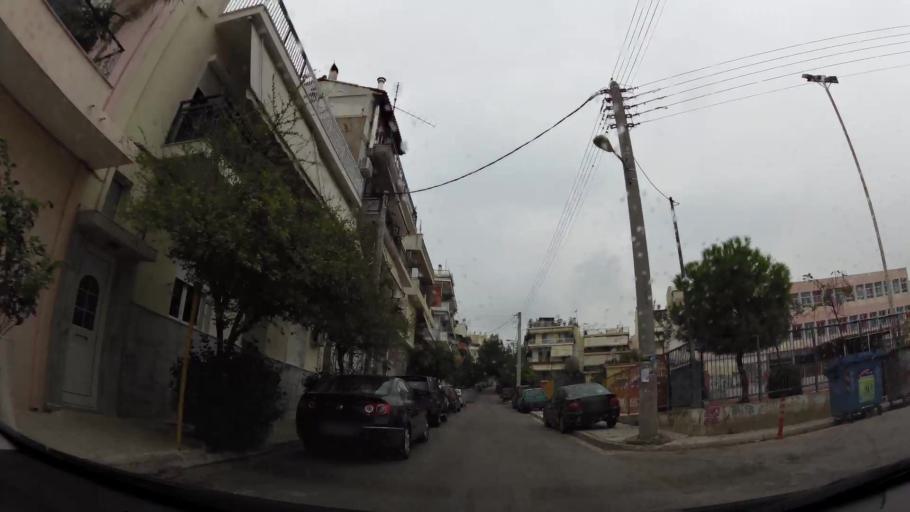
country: GR
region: Attica
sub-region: Nomarchia Athinas
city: Chaidari
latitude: 38.0002
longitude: 23.6704
